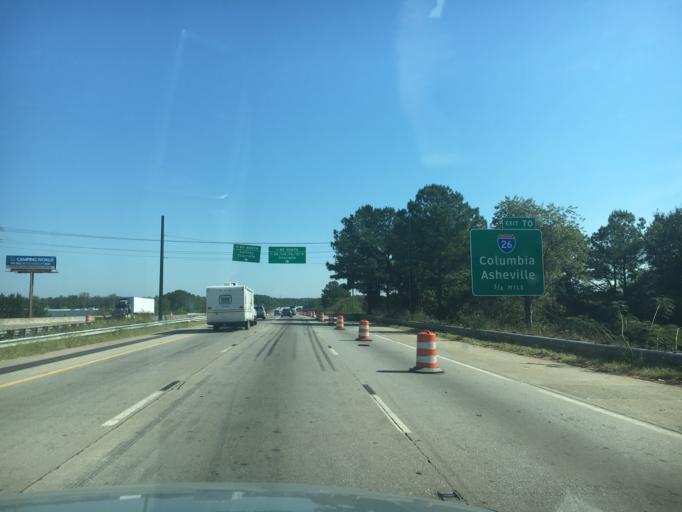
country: US
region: South Carolina
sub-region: Spartanburg County
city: Fairforest
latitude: 34.9666
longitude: -82.0296
